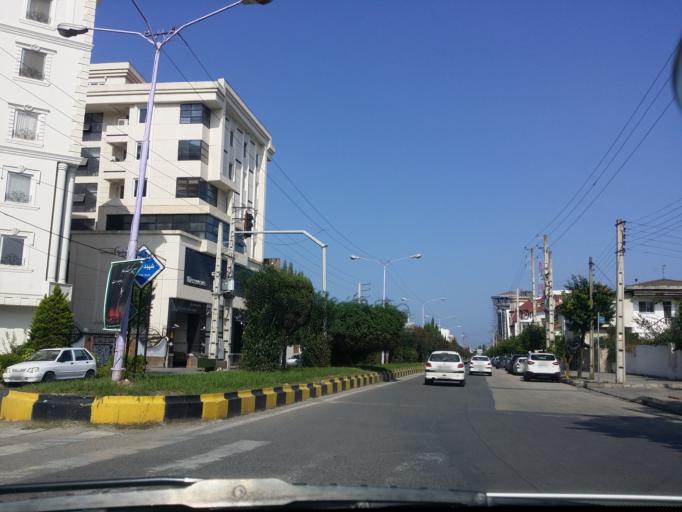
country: IR
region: Mazandaran
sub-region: Nowshahr
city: Nowshahr
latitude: 36.6478
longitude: 51.4932
